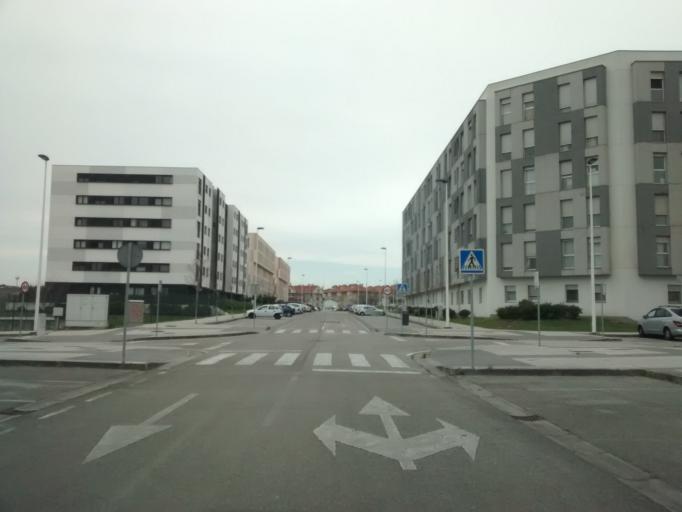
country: ES
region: Cantabria
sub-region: Provincia de Cantabria
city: Camargo
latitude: 43.4402
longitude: -3.8546
